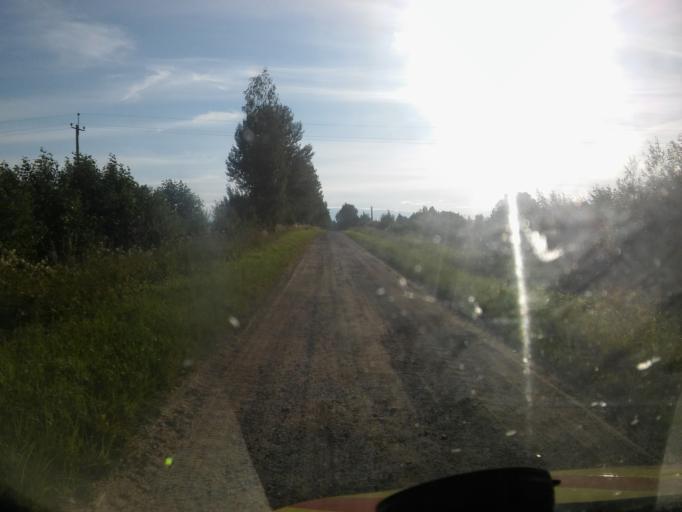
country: EE
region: Valgamaa
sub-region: Torva linn
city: Torva
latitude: 58.0953
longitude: 25.9494
